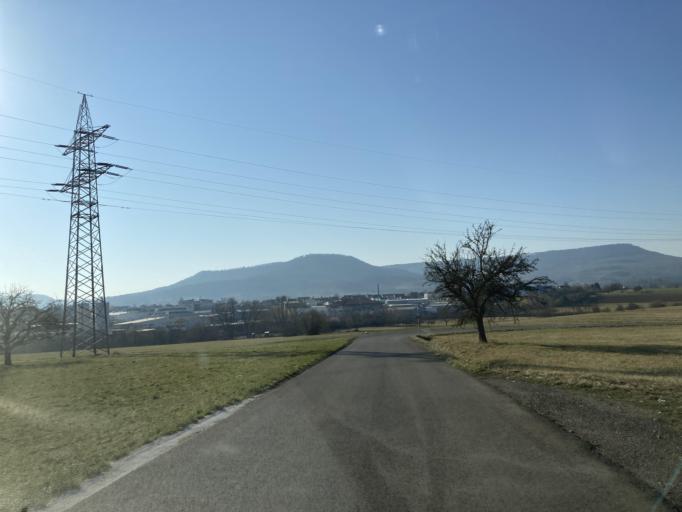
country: DE
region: Baden-Wuerttemberg
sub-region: Tuebingen Region
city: Mossingen
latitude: 48.4178
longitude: 9.0485
